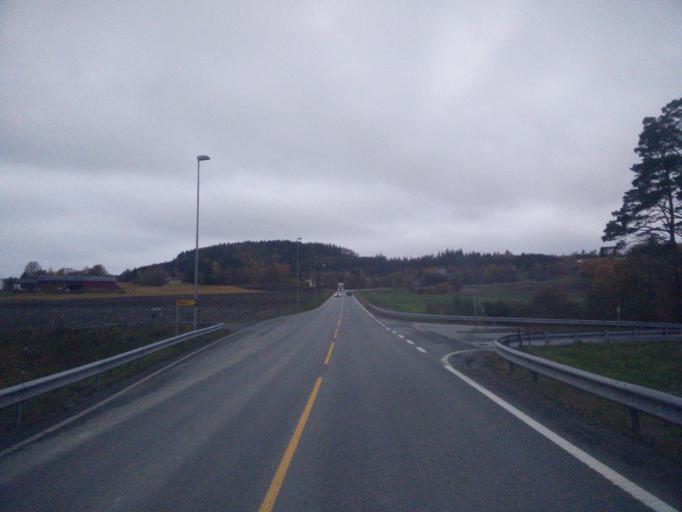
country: NO
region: Nord-Trondelag
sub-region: Stjordal
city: Stjordal
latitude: 63.5059
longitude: 10.8569
